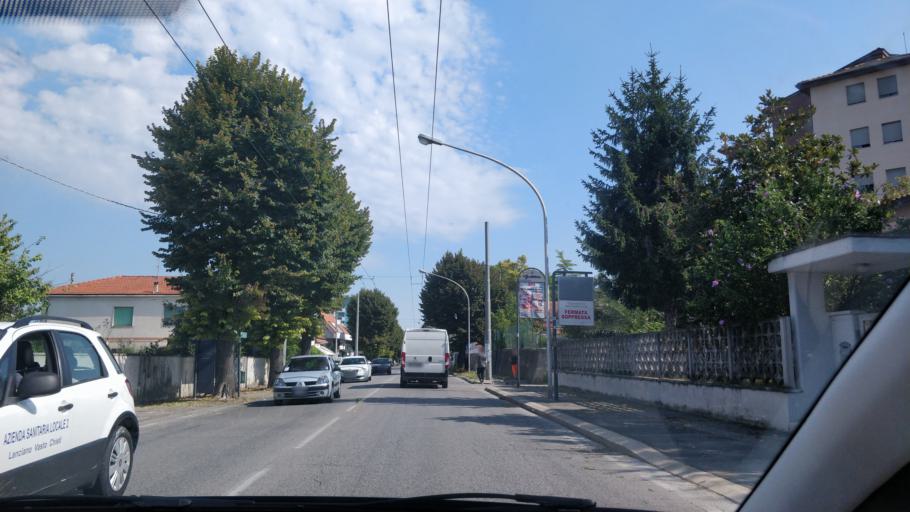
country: IT
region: Abruzzo
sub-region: Provincia di Chieti
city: Chieti
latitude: 42.3809
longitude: 14.1501
